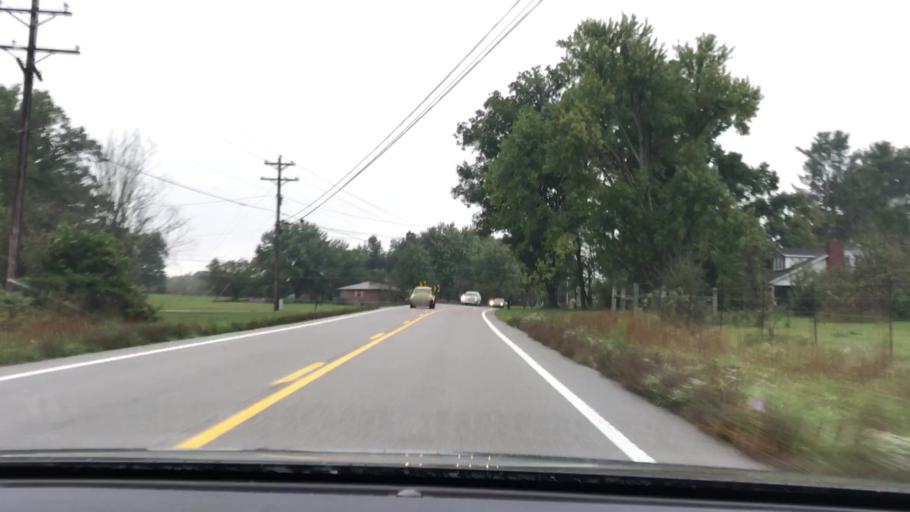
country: US
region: Tennessee
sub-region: Fentress County
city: Grimsley
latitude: 36.2024
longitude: -85.0195
